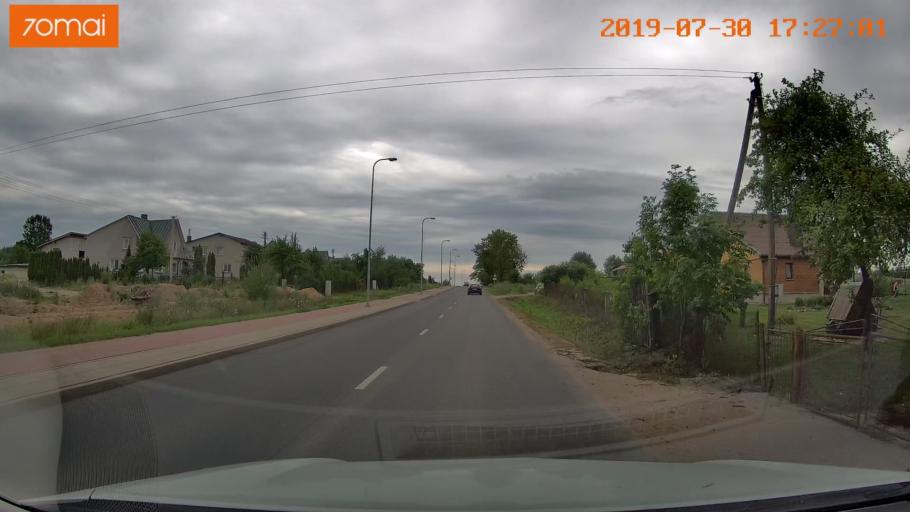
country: LT
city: Skaidiskes
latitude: 54.7163
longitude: 25.4125
